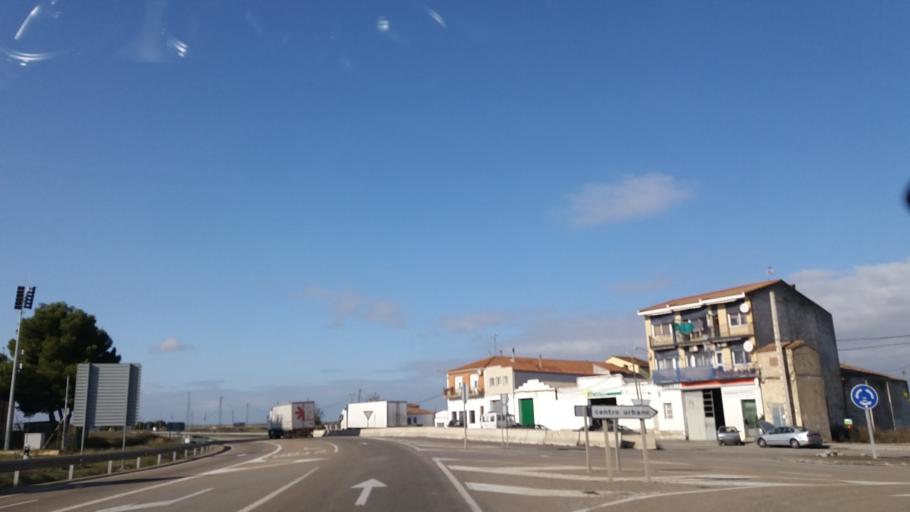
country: ES
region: Aragon
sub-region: Provincia de Zaragoza
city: Bujaraloz
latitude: 41.4972
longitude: -0.1580
